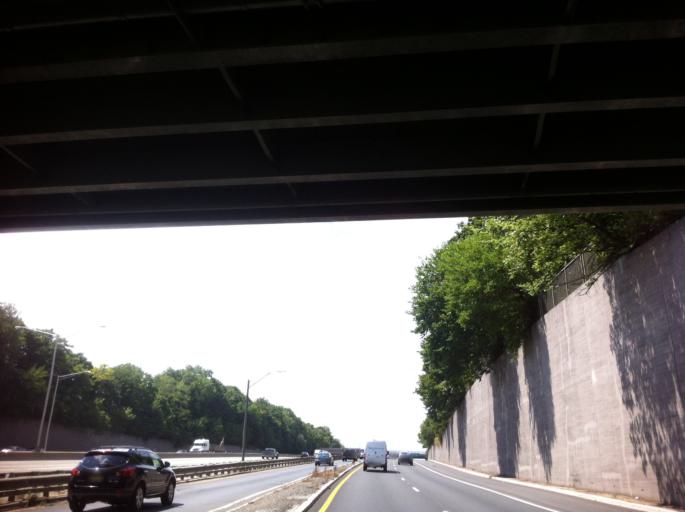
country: US
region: New Jersey
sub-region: Bergen County
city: Ridgefield Park
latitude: 40.8654
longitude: -74.0144
